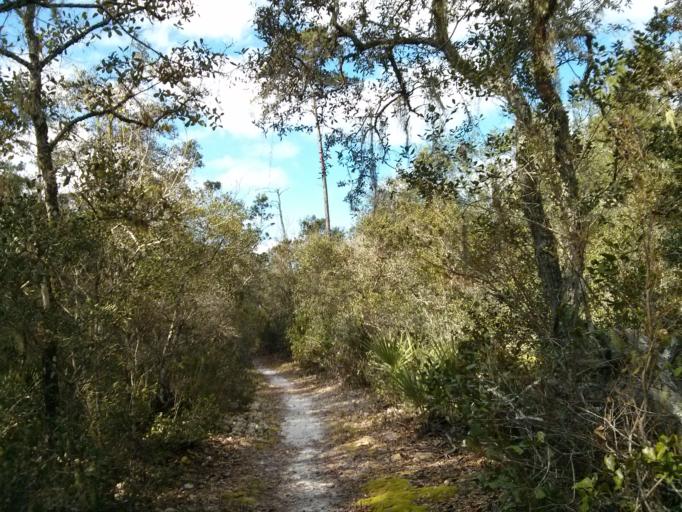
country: US
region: Florida
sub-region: Lake County
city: Astor
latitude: 29.0701
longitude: -81.6186
